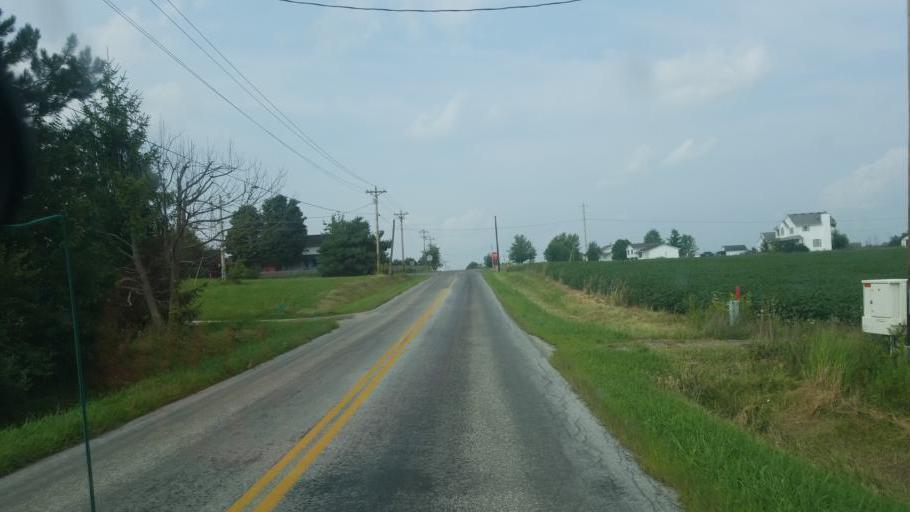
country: US
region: Ohio
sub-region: Wayne County
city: West Salem
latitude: 41.0679
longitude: -82.1621
